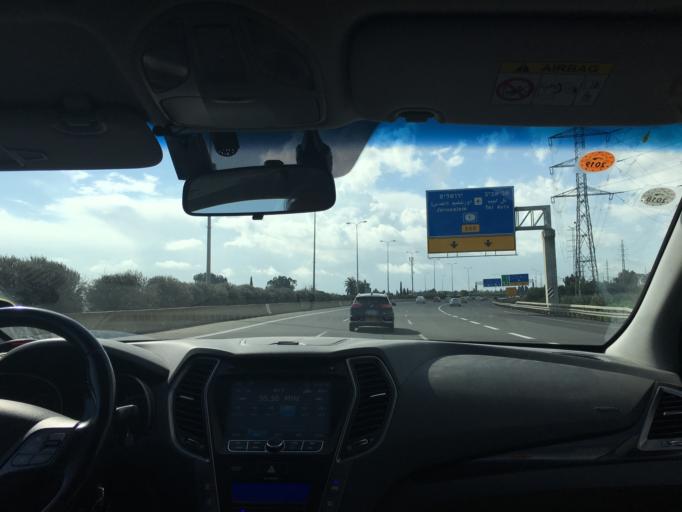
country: IL
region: Tel Aviv
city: Azor
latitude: 32.0301
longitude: 34.8288
